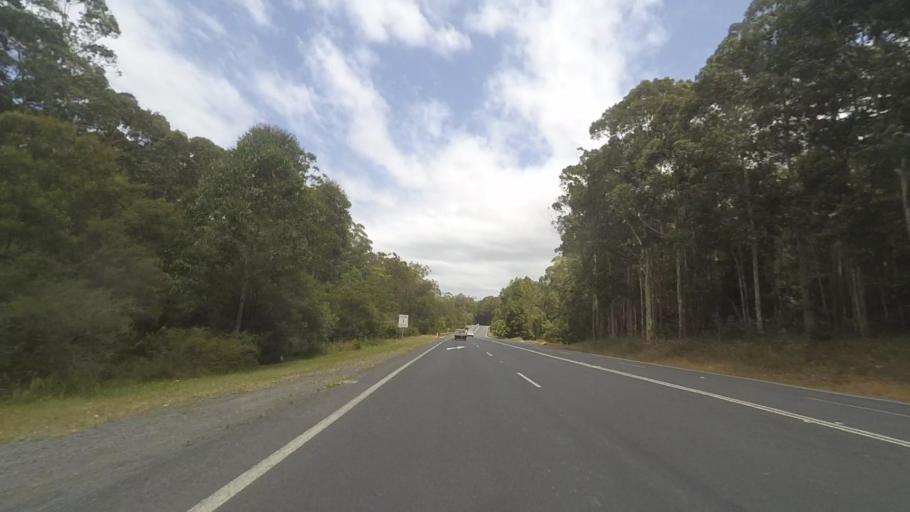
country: AU
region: New South Wales
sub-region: Shoalhaven Shire
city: Falls Creek
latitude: -35.0751
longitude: 150.5601
